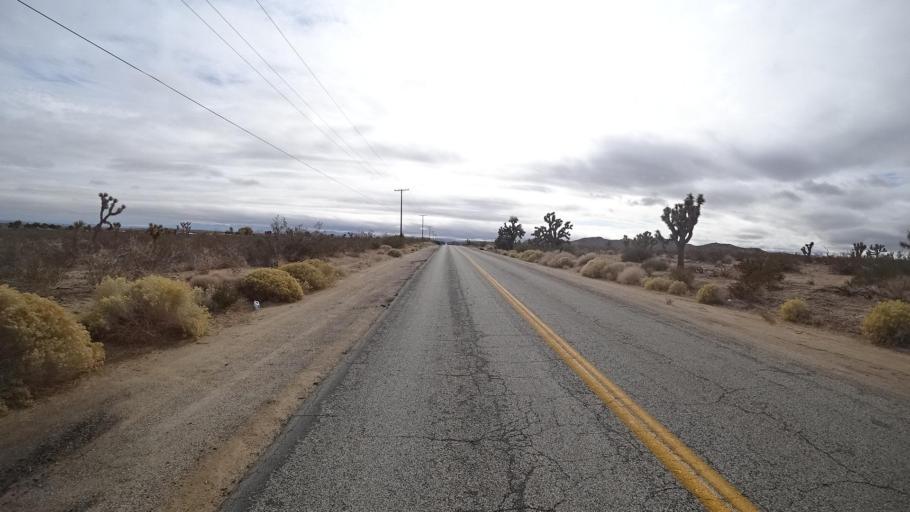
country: US
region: California
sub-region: Kern County
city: Rosamond
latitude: 34.9549
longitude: -118.2127
